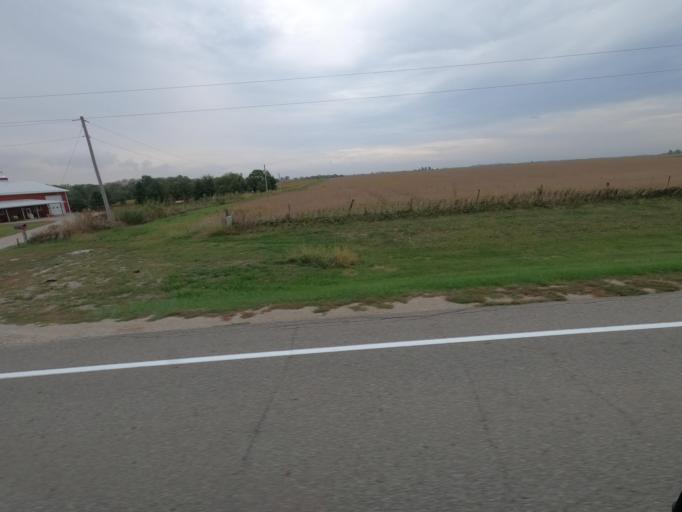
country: US
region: Iowa
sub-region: Van Buren County
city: Keosauqua
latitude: 40.8133
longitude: -91.7902
